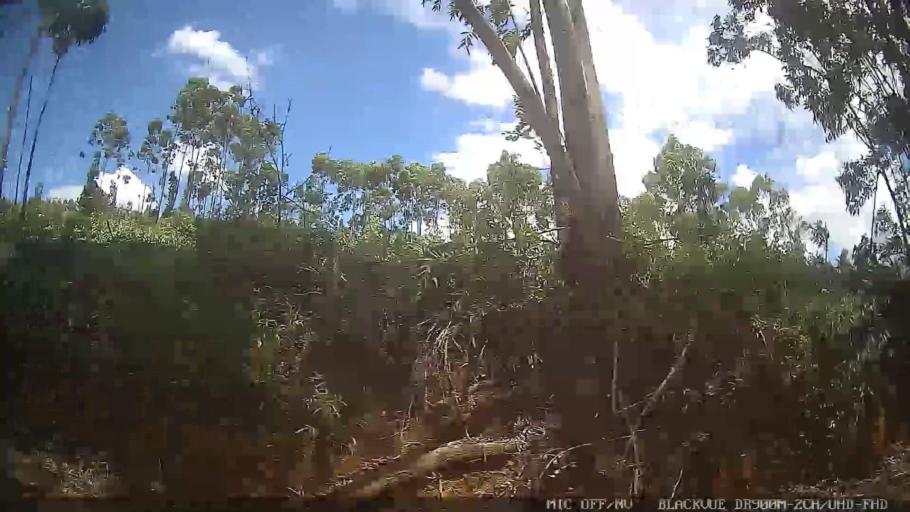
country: BR
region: Minas Gerais
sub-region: Extrema
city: Extrema
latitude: -22.7492
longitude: -46.4330
